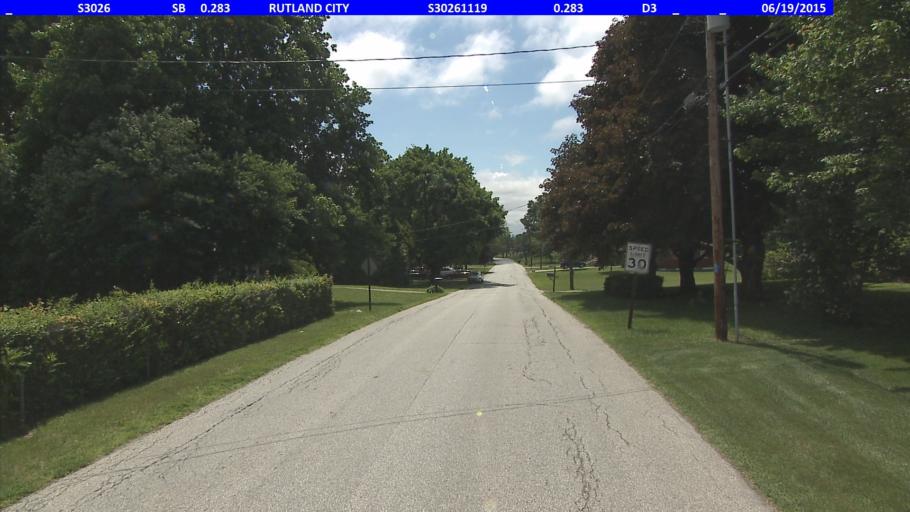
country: US
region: Vermont
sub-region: Rutland County
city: Rutland
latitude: 43.6210
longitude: -72.9603
